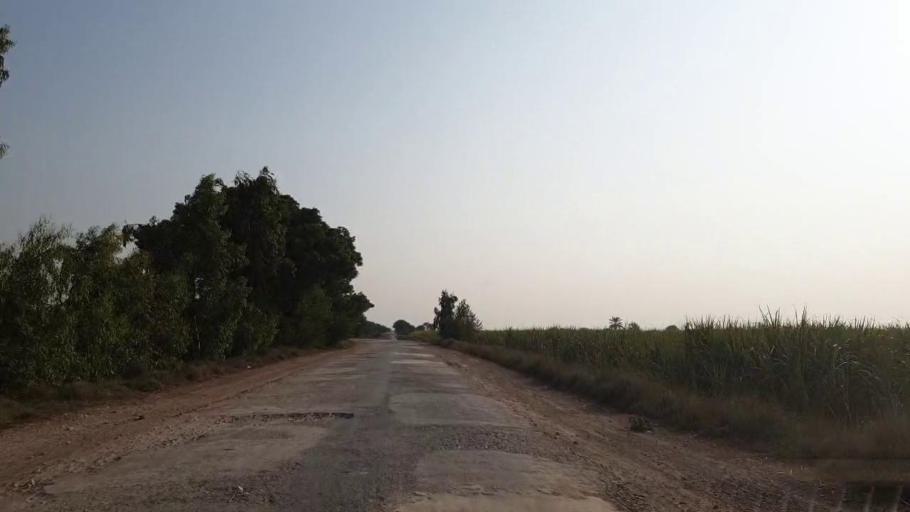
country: PK
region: Sindh
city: Bulri
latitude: 24.9817
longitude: 68.3918
